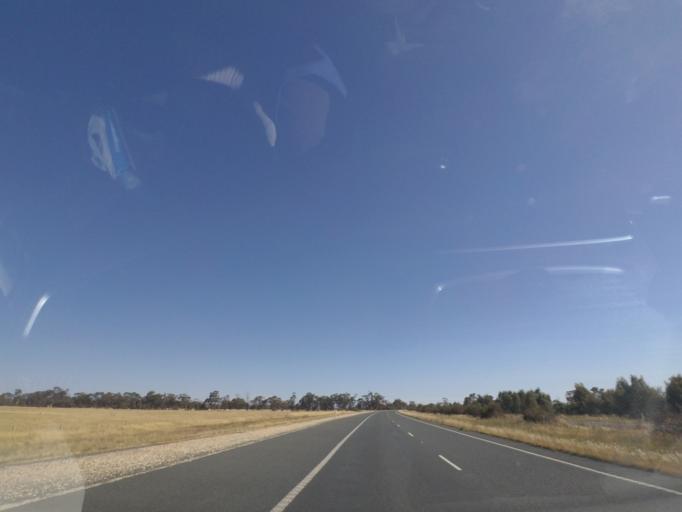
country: AU
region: Victoria
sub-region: Greater Shepparton
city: Shepparton
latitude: -36.7997
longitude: 145.1785
